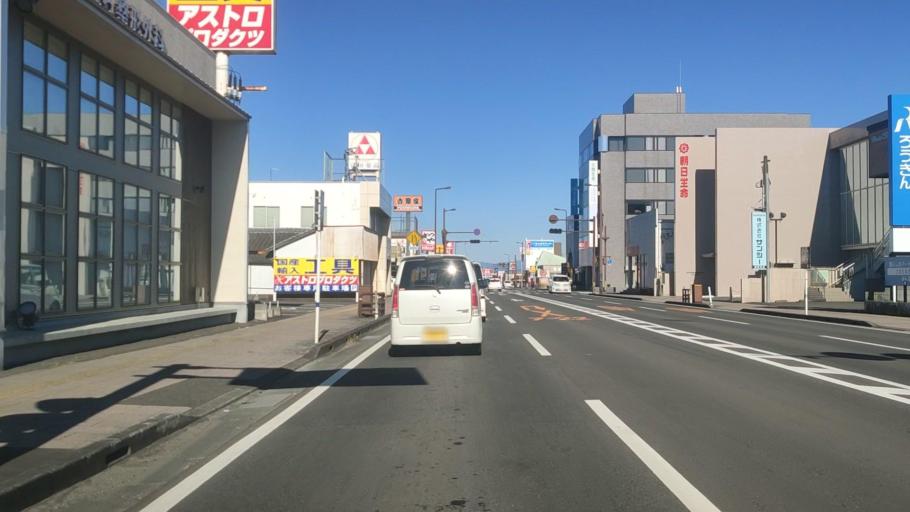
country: JP
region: Miyazaki
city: Miyakonojo
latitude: 31.7329
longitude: 131.0685
